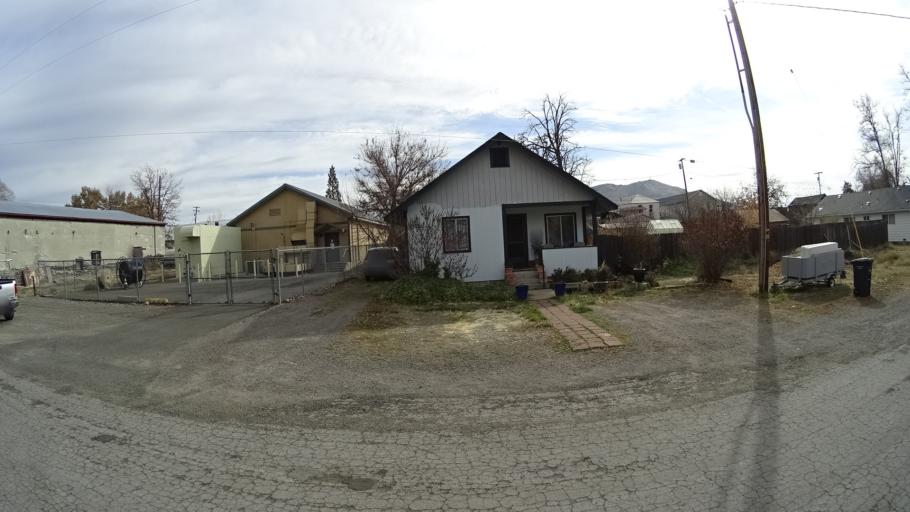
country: US
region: California
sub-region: Siskiyou County
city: Montague
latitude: 41.7283
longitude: -122.5292
